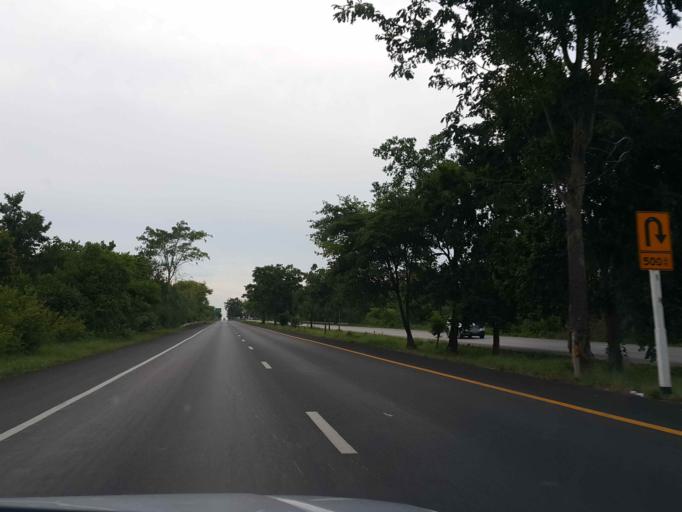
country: TH
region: Lampang
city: Ko Kha
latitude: 18.0865
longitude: 99.3954
